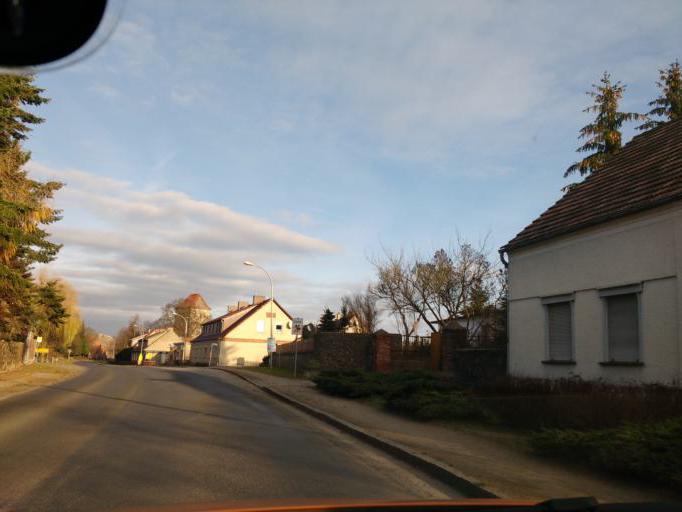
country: DE
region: Brandenburg
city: Wriezen
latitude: 52.6862
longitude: 14.0974
